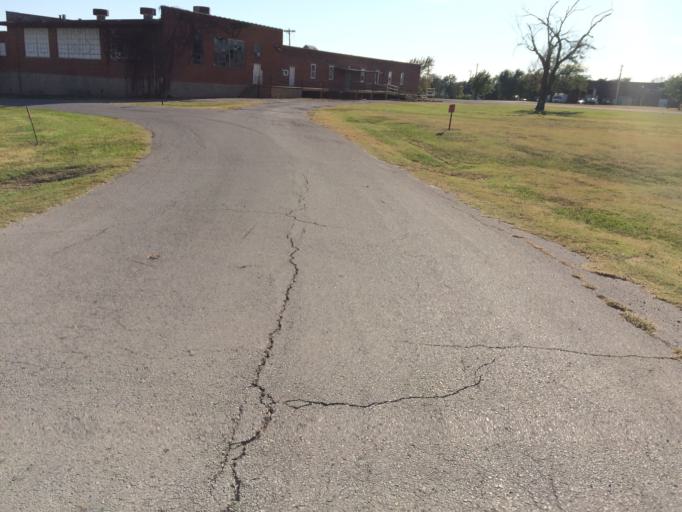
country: US
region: Oklahoma
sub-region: Cleveland County
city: Norman
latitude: 35.2271
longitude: -97.4267
